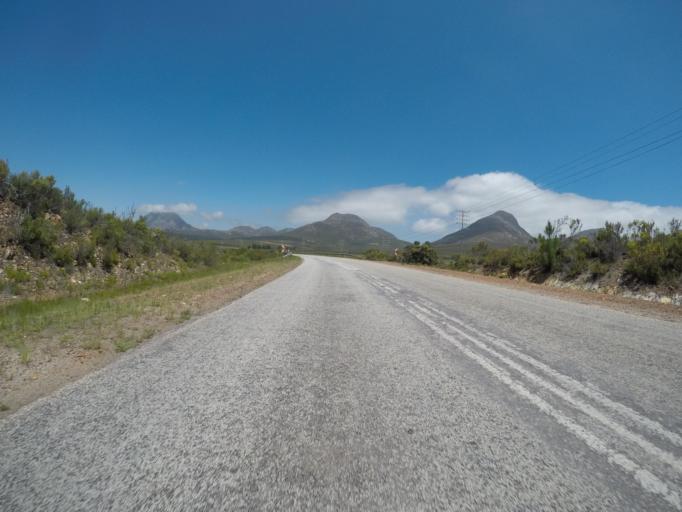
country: ZA
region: Eastern Cape
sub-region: Cacadu District Municipality
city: Kareedouw
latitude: -33.9404
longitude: 24.2662
